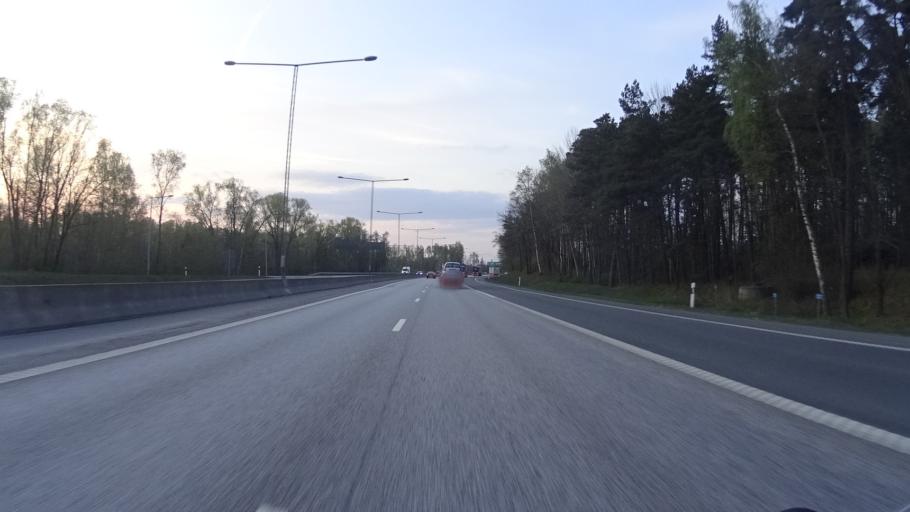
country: SE
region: Joenkoeping
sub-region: Jonkopings Kommun
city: Jonkoping
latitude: 57.7656
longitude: 14.1895
